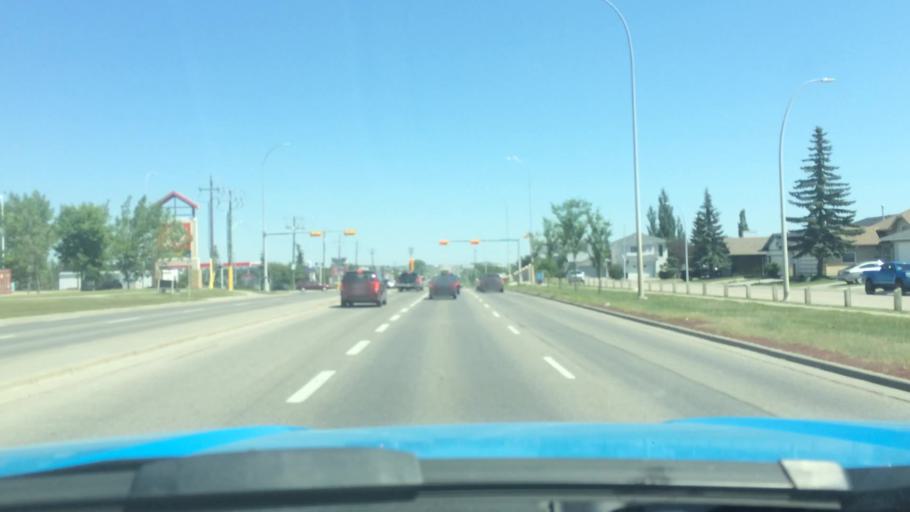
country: CA
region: Alberta
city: Calgary
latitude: 51.1541
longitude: -114.0625
